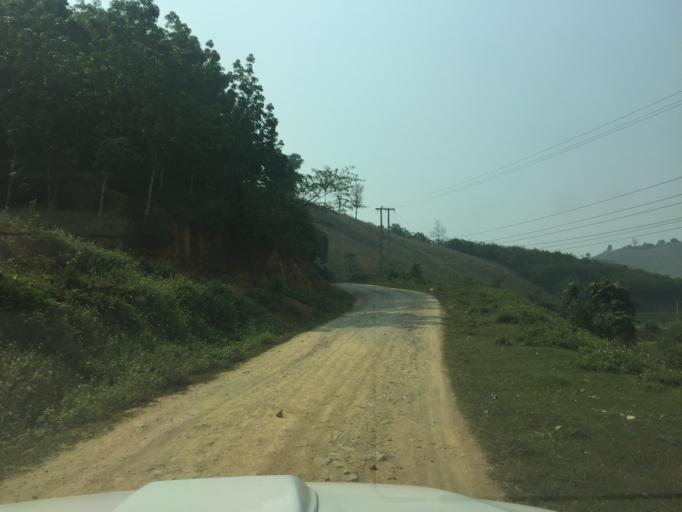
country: TH
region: Phayao
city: Phu Sang
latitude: 19.6202
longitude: 100.5388
